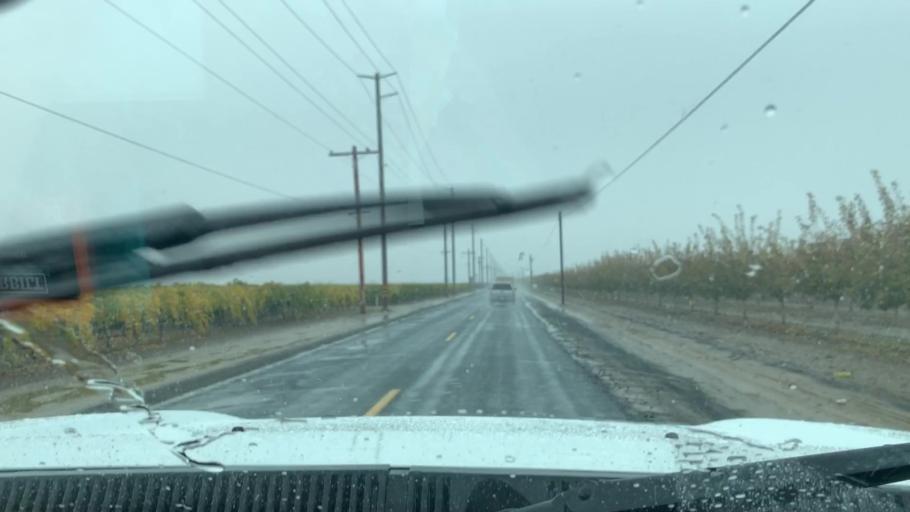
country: US
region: California
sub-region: Kern County
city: Delano
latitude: 35.8340
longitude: -119.2251
